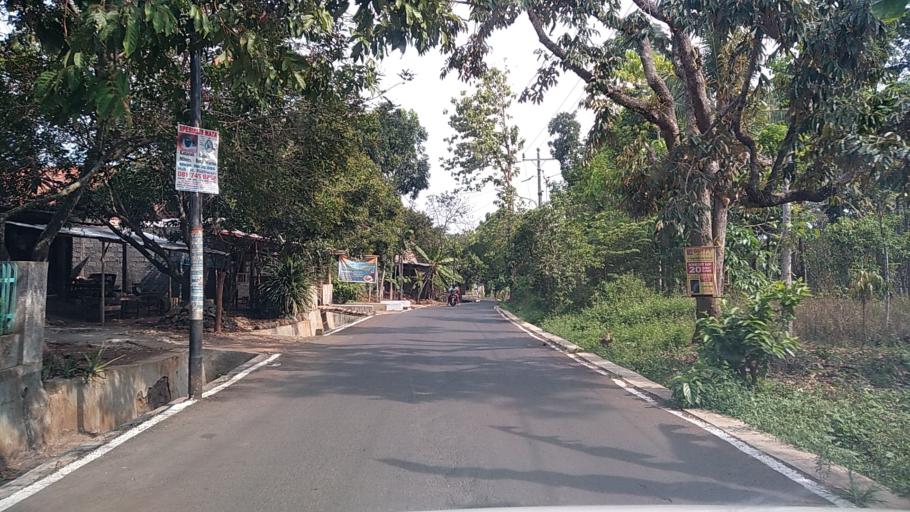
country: ID
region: Central Java
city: Semarang
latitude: -7.0202
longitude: 110.3096
